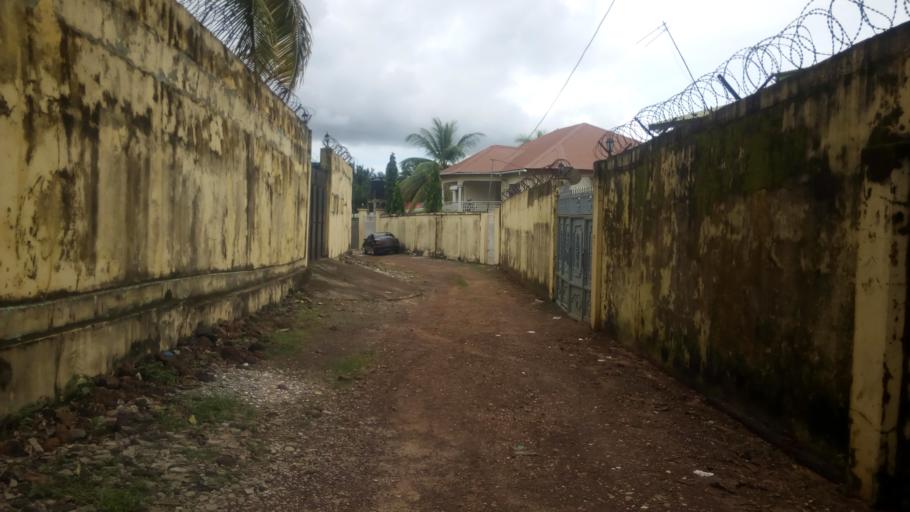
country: GN
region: Conakry
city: Conakry
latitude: 9.5985
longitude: -13.6550
